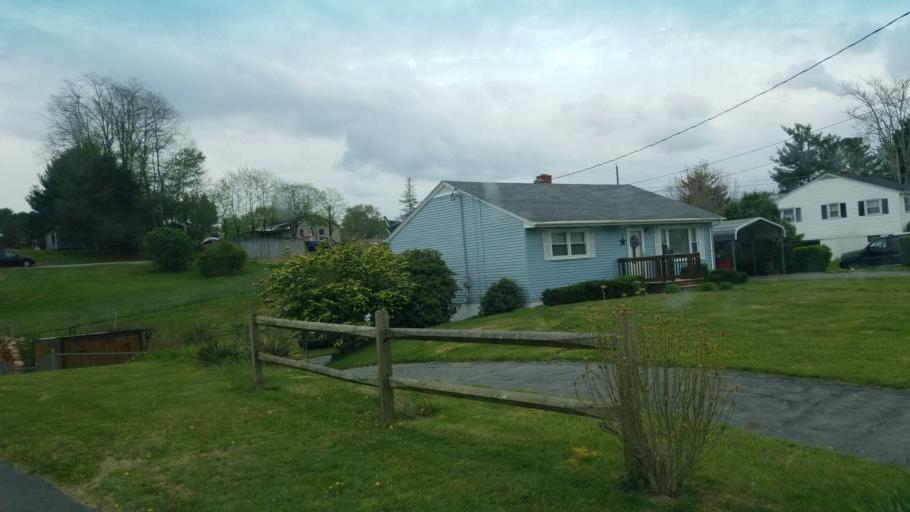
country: US
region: Virginia
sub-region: Smyth County
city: Adwolf
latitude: 36.8181
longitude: -81.5743
